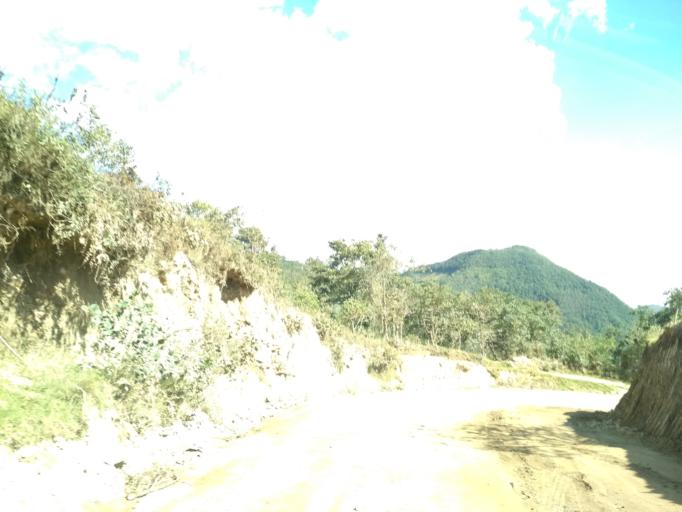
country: CO
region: Cauca
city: Jambalo
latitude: 2.7071
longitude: -76.3287
